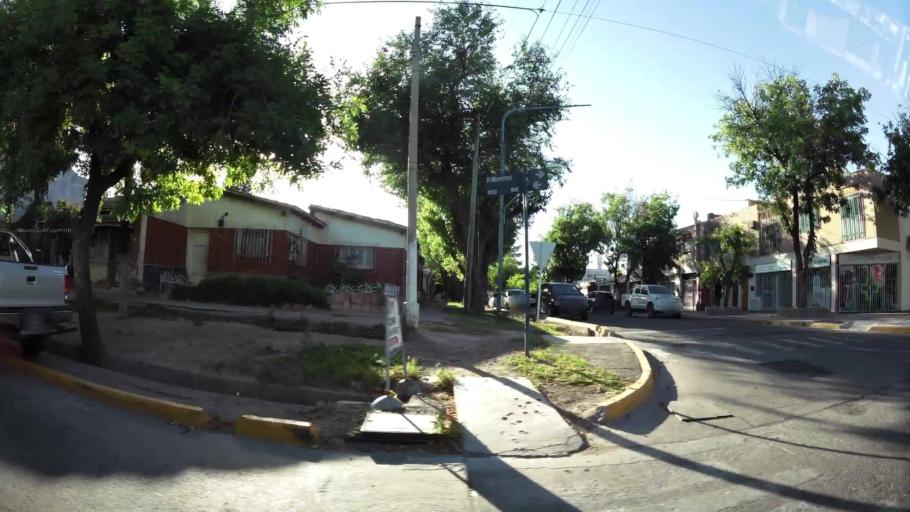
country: AR
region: Mendoza
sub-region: Departamento de Godoy Cruz
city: Godoy Cruz
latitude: -32.9424
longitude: -68.8483
